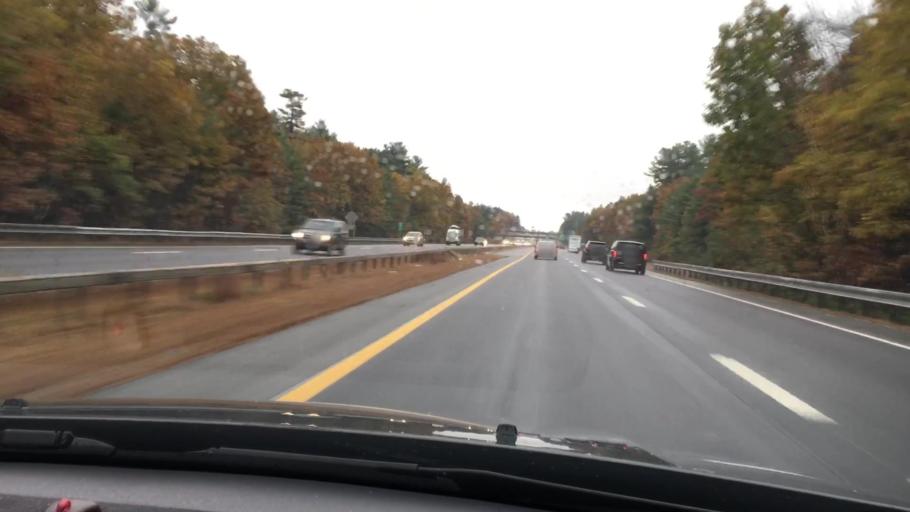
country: US
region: New Hampshire
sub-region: Hillsborough County
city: Nashua
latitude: 42.7979
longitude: -71.4976
